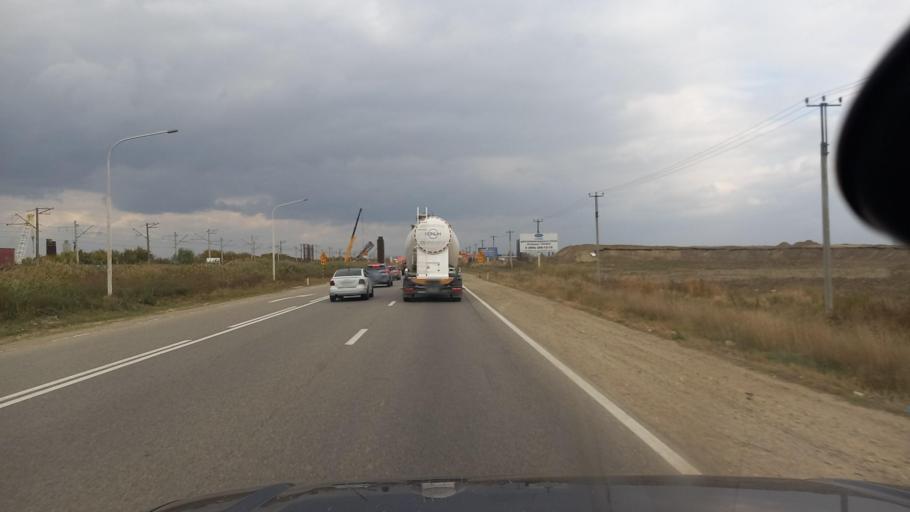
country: RU
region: Adygeya
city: Enem
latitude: 44.9397
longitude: 38.9168
